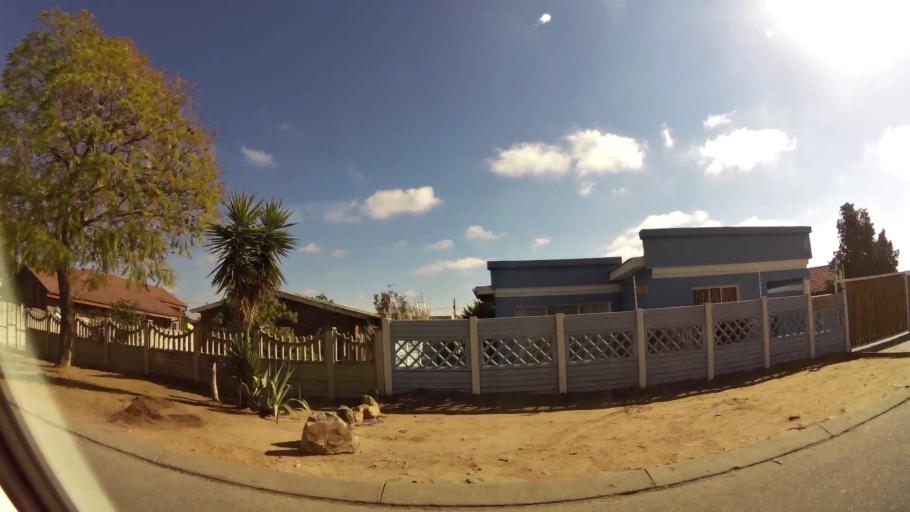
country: ZA
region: Limpopo
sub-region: Capricorn District Municipality
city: Polokwane
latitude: -23.8573
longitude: 29.3649
